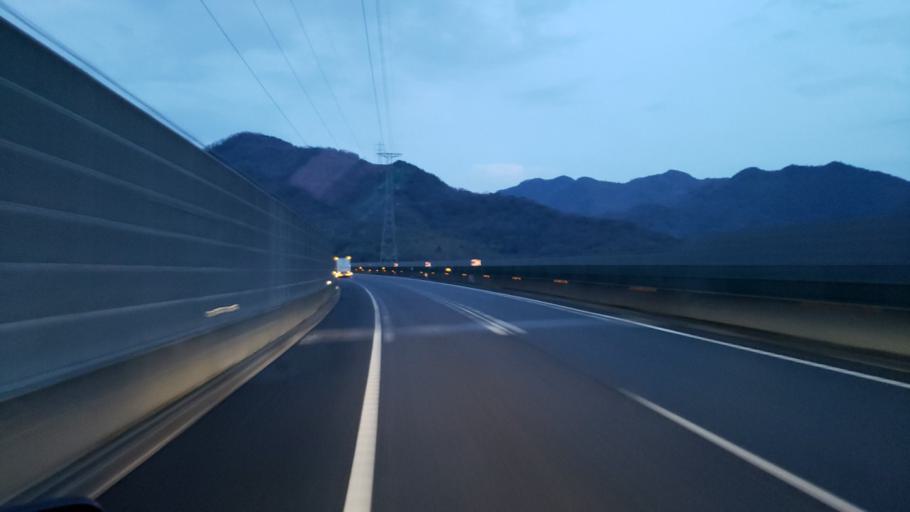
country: JP
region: Hyogo
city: Himeji
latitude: 34.8494
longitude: 134.7519
